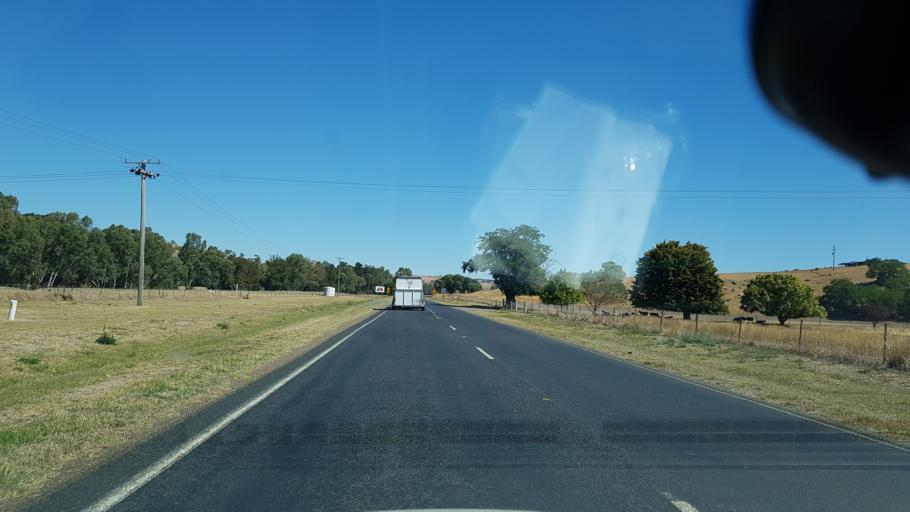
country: AU
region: New South Wales
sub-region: Gundagai
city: Gundagai
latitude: -34.8214
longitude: 148.3510
